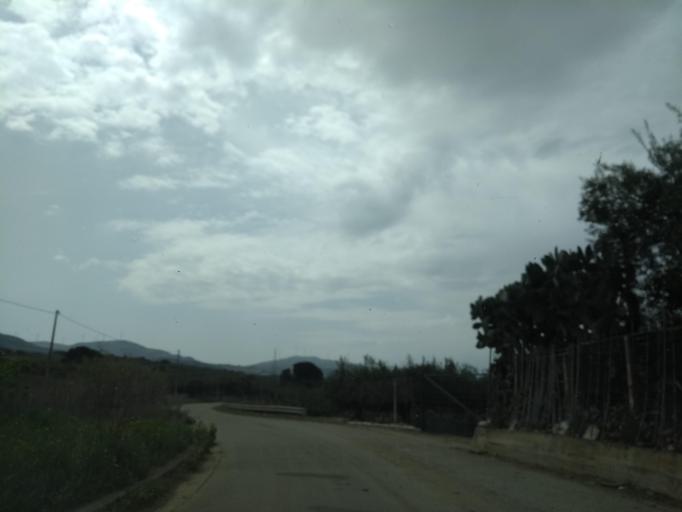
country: IT
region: Sicily
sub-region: Palermo
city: Partinico
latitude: 37.9944
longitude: 13.0771
